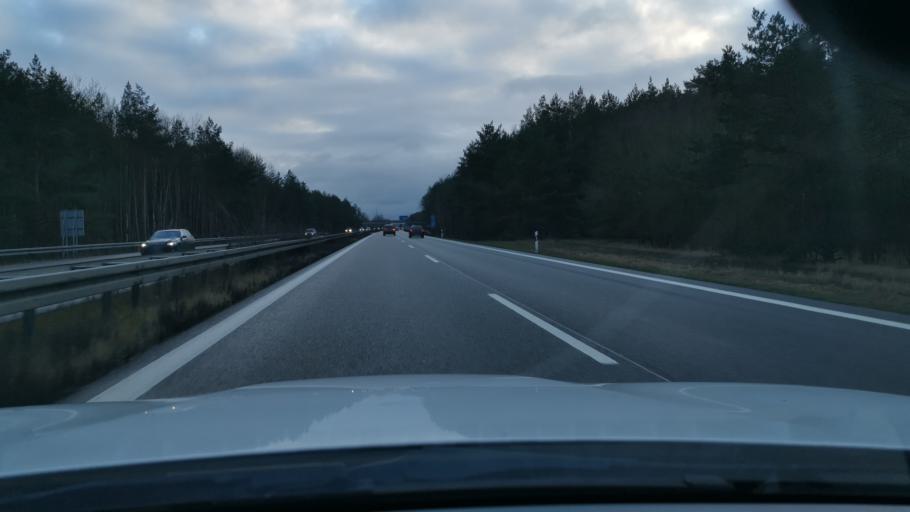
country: DE
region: Brandenburg
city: Brieselang
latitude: 52.6230
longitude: 12.9806
